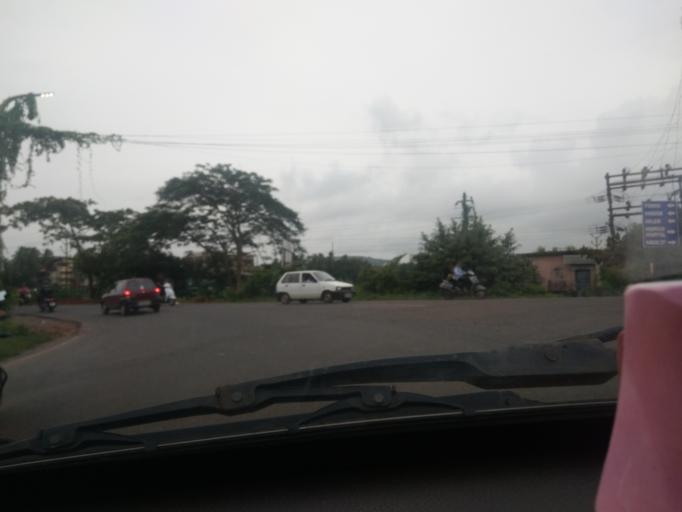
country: IN
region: Goa
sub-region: South Goa
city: Madgaon
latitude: 15.2862
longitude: 73.9636
